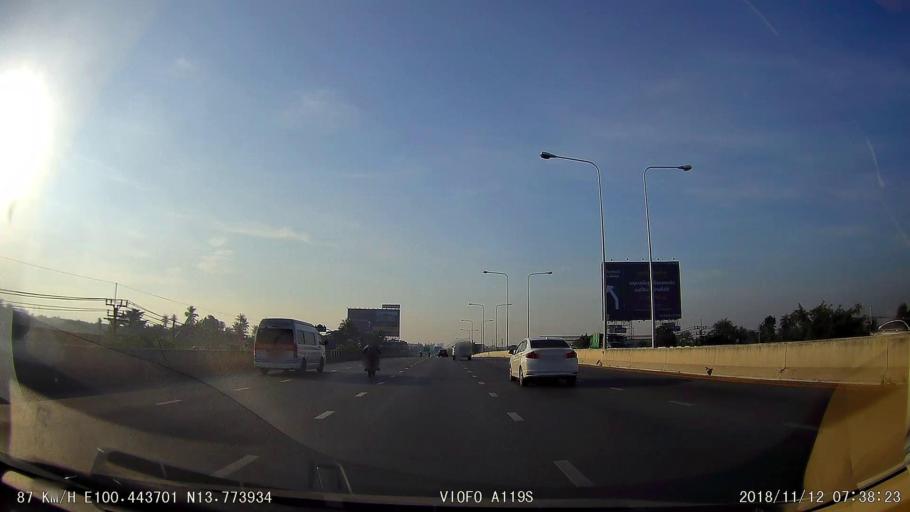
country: TH
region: Bangkok
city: Taling Chan
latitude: 13.7746
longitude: 100.4437
